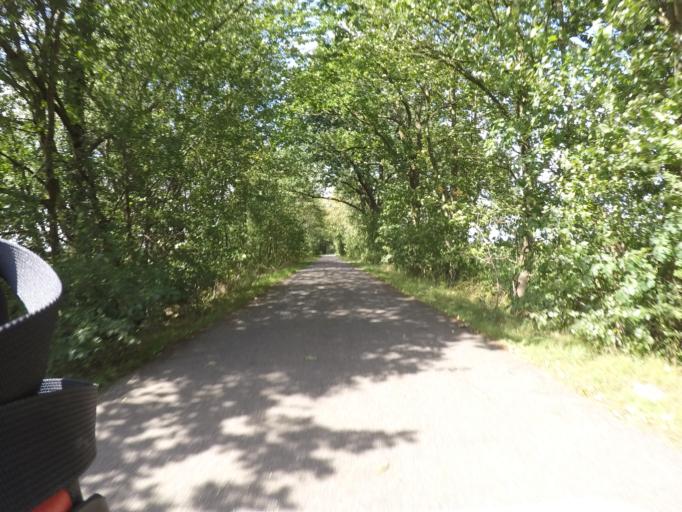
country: DE
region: Lower Saxony
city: Stelle
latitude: 53.4312
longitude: 10.1464
